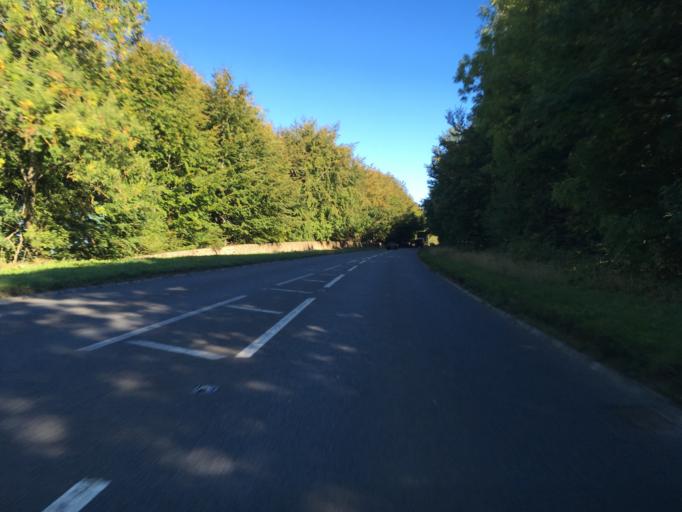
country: GB
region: England
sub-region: South Gloucestershire
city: Hinton
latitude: 51.5115
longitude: -2.3433
